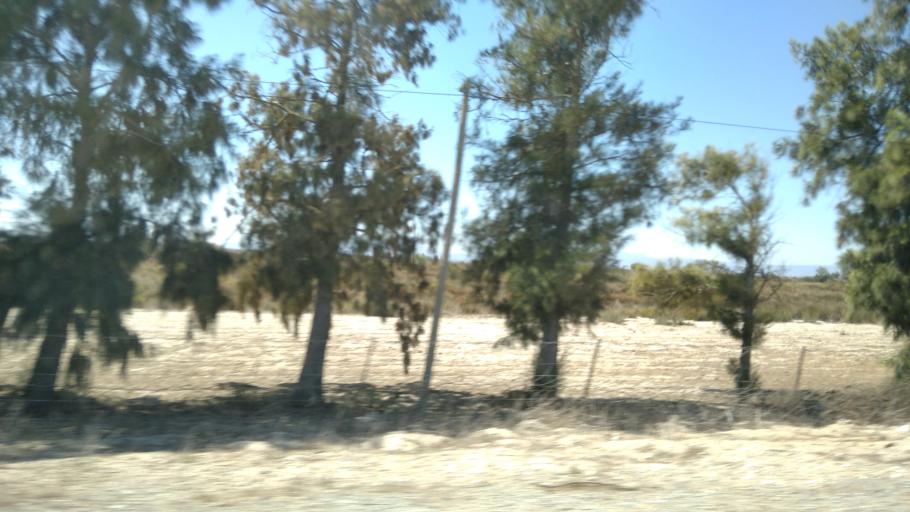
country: ZA
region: Western Cape
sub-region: West Coast District Municipality
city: Vredenburg
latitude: -33.0411
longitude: 18.3109
